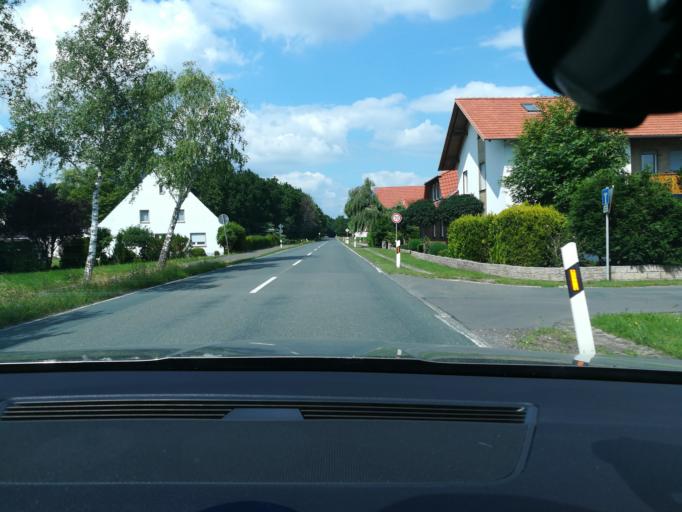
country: DE
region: North Rhine-Westphalia
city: Espelkamp
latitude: 52.3644
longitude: 8.6791
